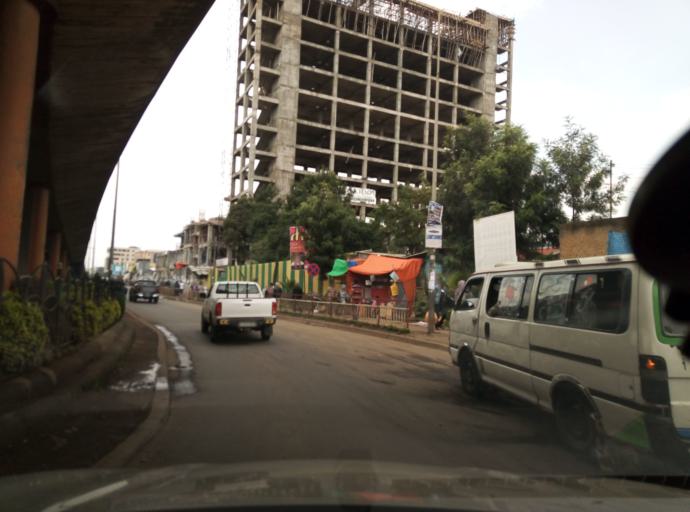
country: ET
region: Adis Abeba
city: Addis Ababa
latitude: 9.0107
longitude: 38.7208
